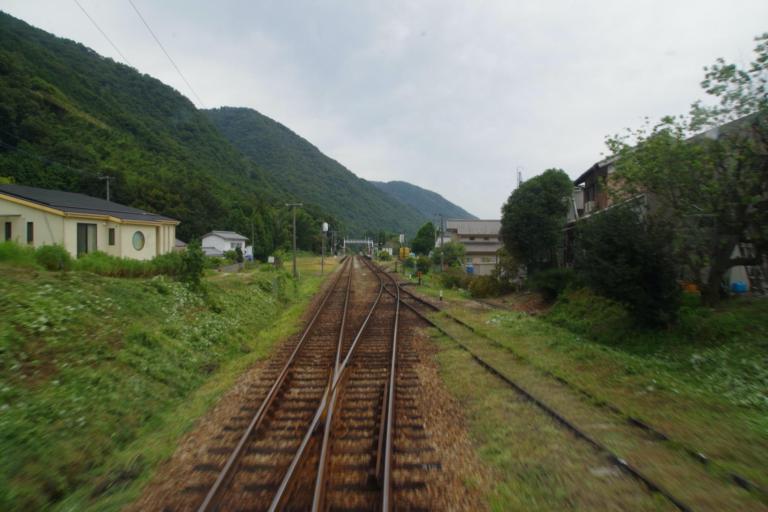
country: JP
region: Tokushima
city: Ikedacho
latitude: 34.0397
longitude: 133.8472
